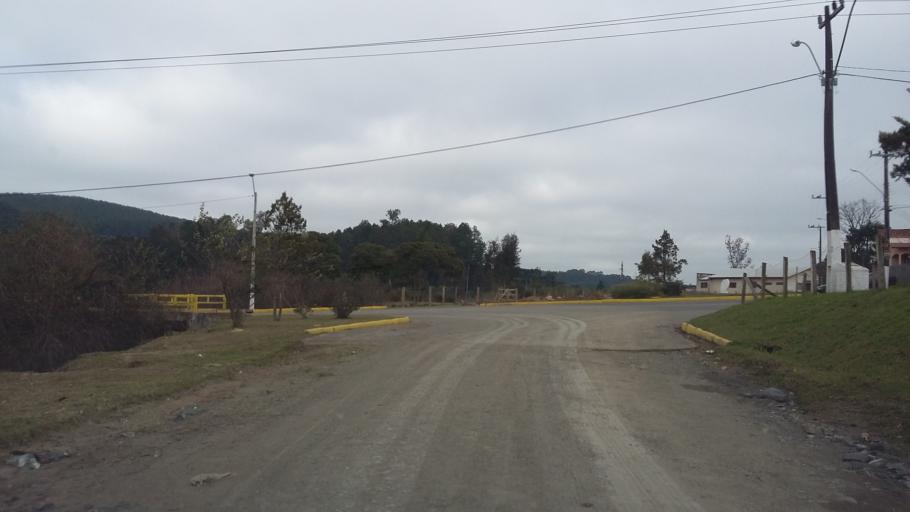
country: BR
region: Santa Catarina
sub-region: Lages
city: Lages
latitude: -27.8384
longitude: -50.3226
